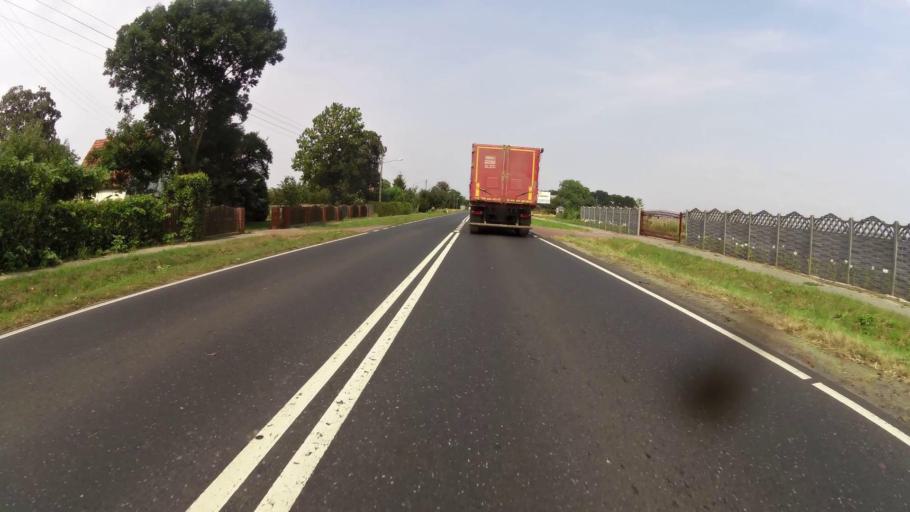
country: PL
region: West Pomeranian Voivodeship
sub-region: Powiat pyrzycki
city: Lipiany
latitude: 52.9542
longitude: 14.9602
